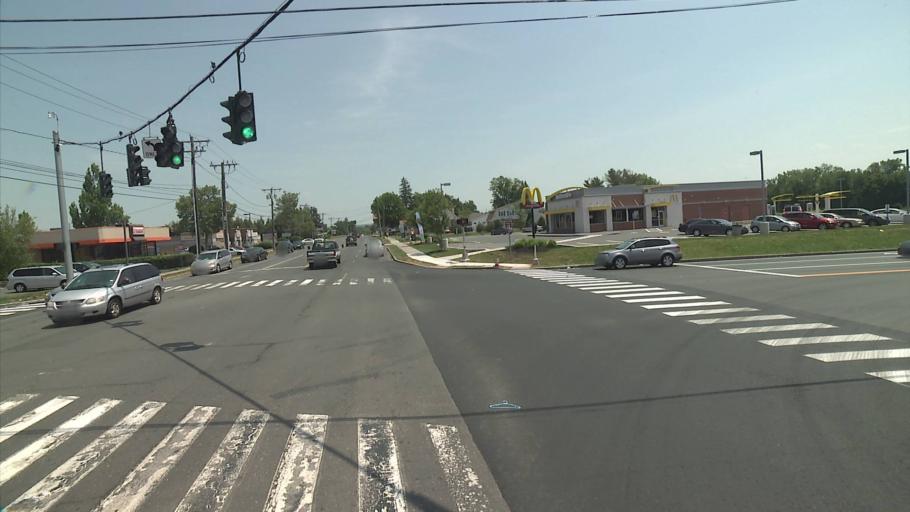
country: US
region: Connecticut
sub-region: Hartford County
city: East Hartford
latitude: 41.7670
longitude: -72.5691
